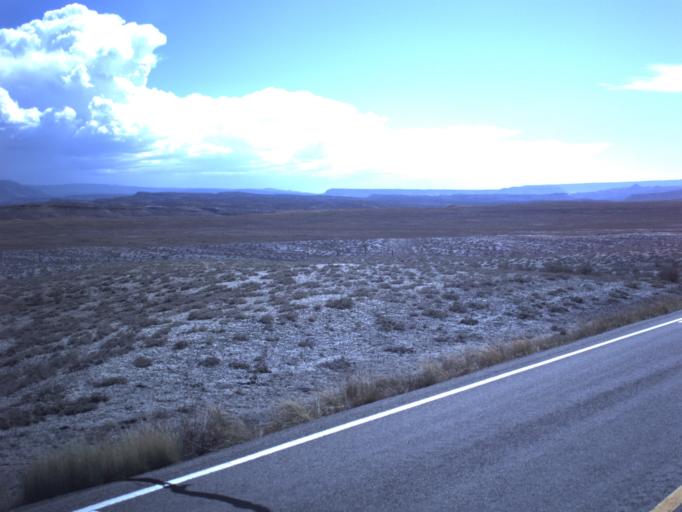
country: US
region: Utah
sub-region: Grand County
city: Moab
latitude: 38.8961
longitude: -109.3117
